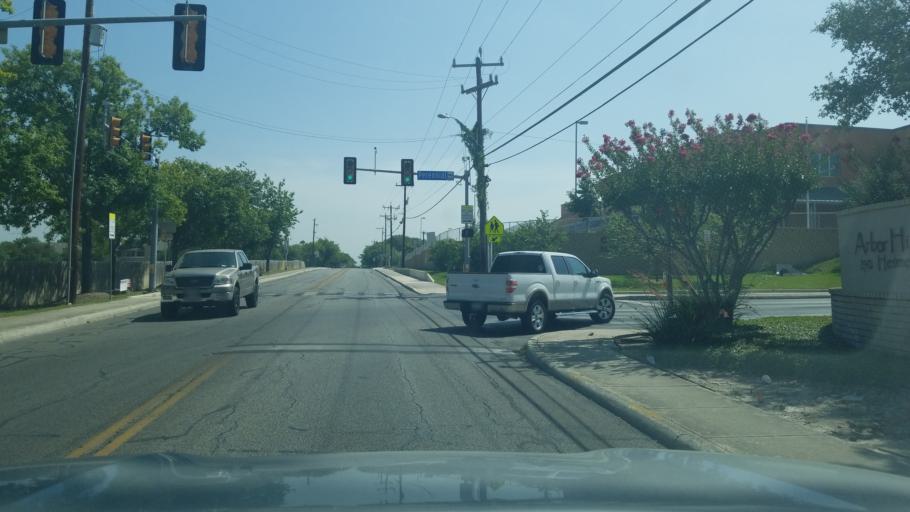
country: US
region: Texas
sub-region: Bexar County
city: Hollywood Park
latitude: 29.5658
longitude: -98.4773
